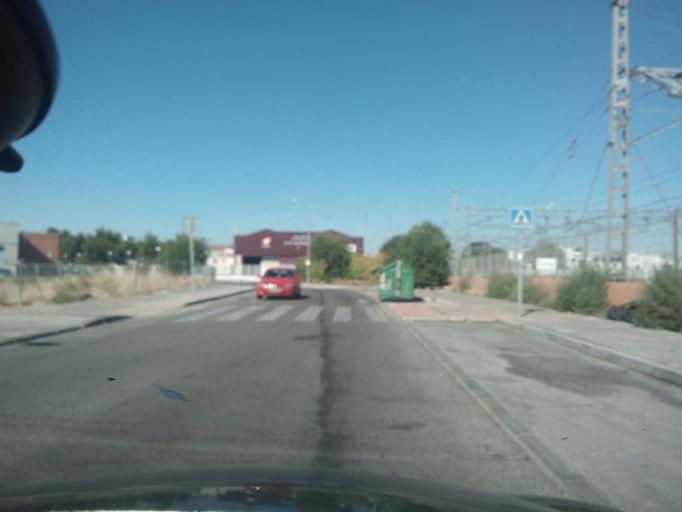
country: ES
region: Madrid
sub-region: Provincia de Madrid
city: Torrejon de Ardoz
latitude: 40.4537
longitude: -3.4844
